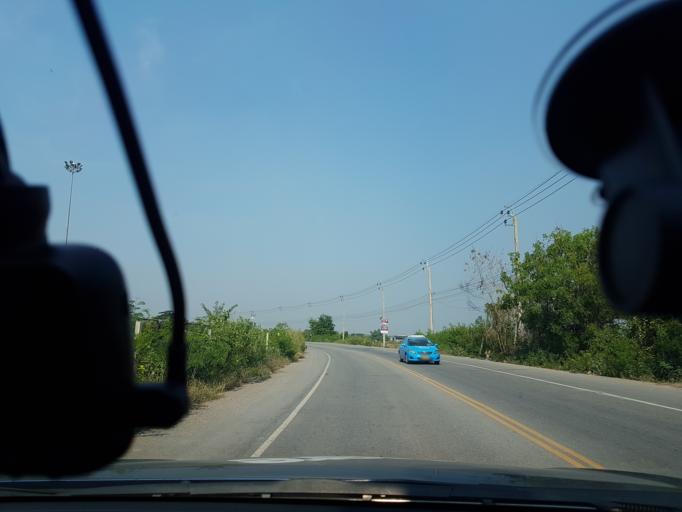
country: TH
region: Bangkok
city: Sai Mai
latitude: 13.8991
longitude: 100.6965
